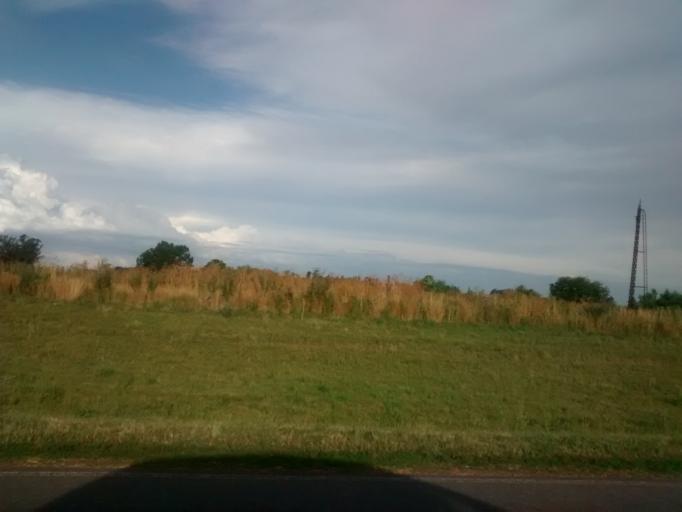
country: AR
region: Buenos Aires
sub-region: Partido de Loberia
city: Loberia
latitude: -38.2057
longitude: -58.7353
